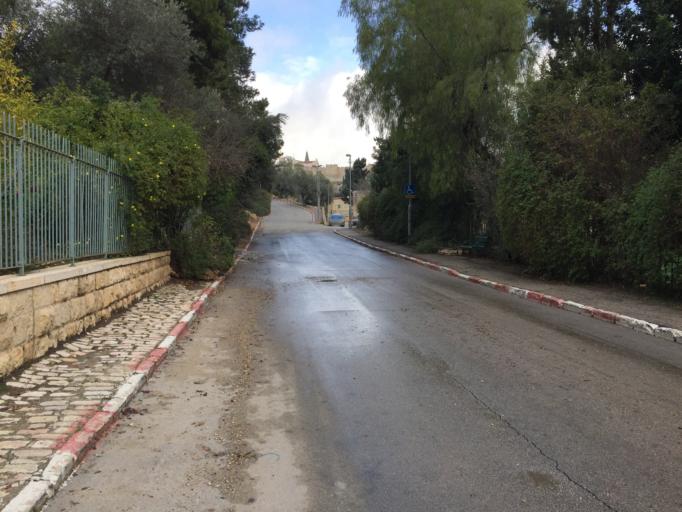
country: PS
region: West Bank
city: Old City
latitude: 31.7736
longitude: 35.2259
